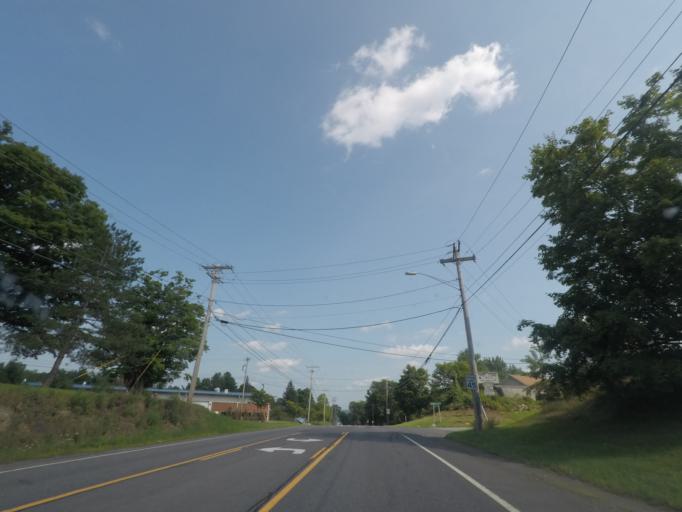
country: US
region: New York
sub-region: Rensselaer County
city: Nassau
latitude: 42.5241
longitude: -73.6420
